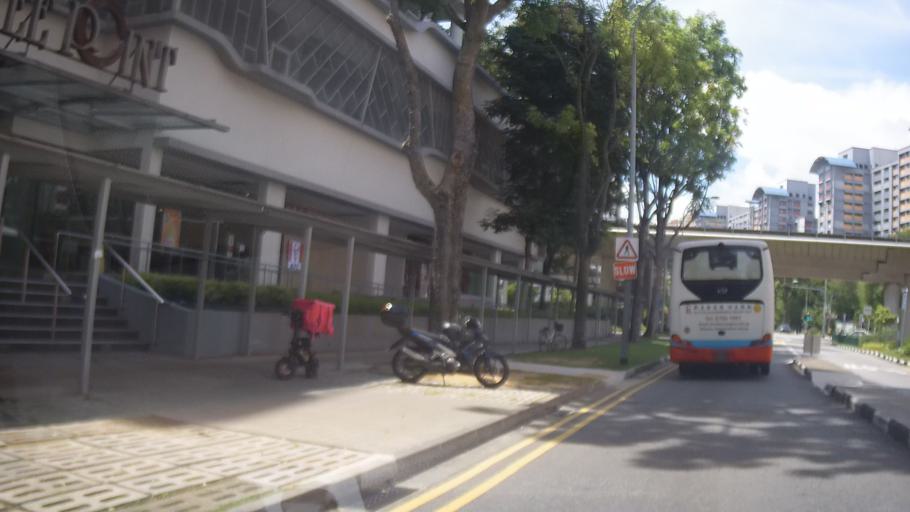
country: MY
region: Johor
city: Johor Bahru
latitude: 1.3966
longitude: 103.7464
